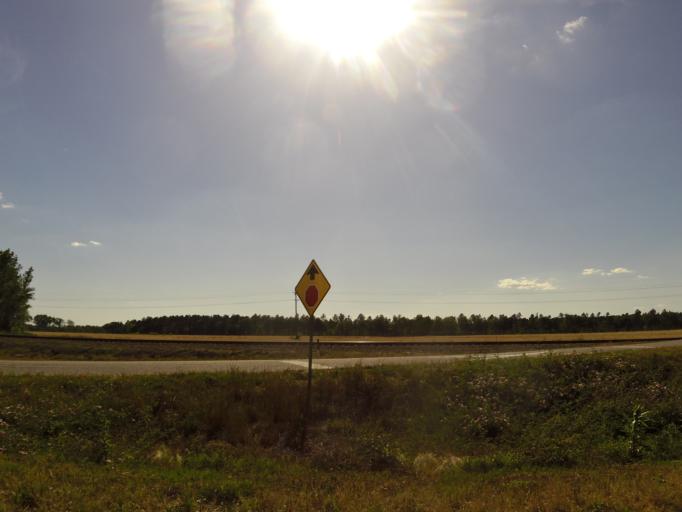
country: US
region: South Carolina
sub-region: Allendale County
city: Fairfax
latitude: 33.0305
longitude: -81.2232
